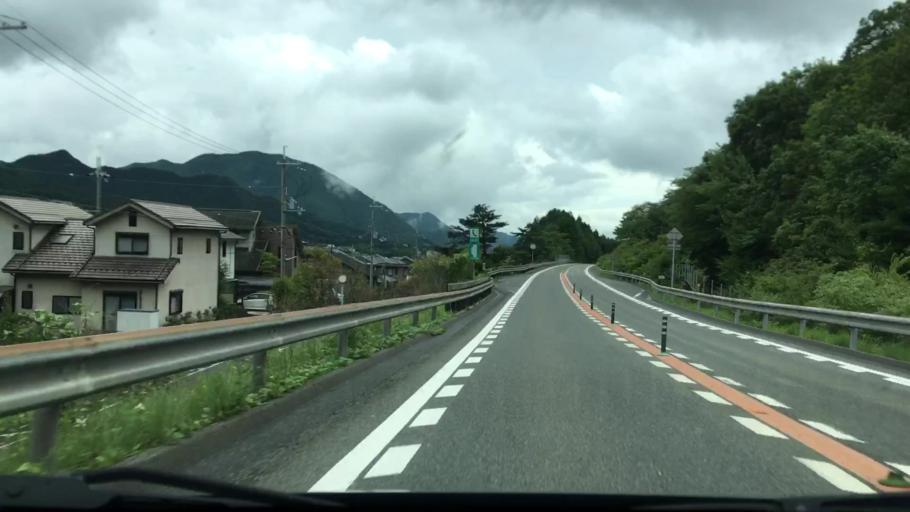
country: JP
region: Hyogo
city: Nishiwaki
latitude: 35.0738
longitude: 134.7704
